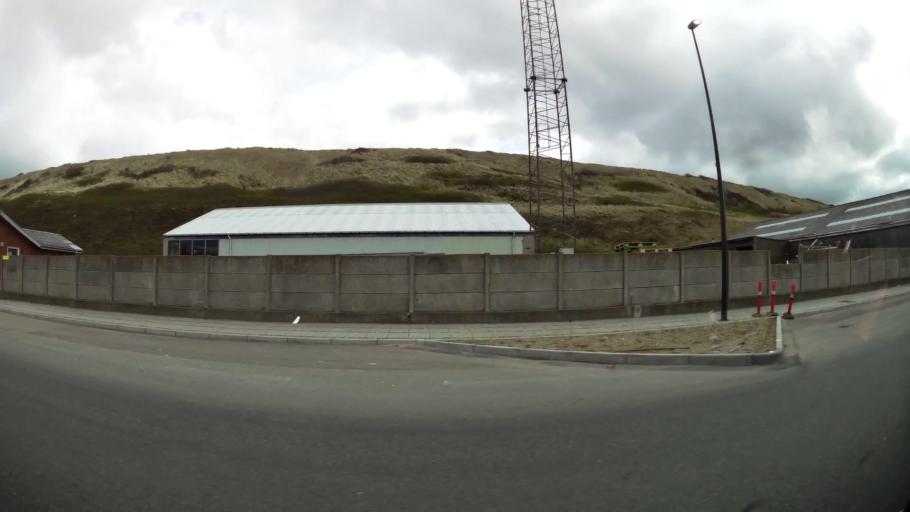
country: DK
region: North Denmark
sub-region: Thisted Kommune
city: Hanstholm
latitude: 57.1207
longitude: 8.6042
